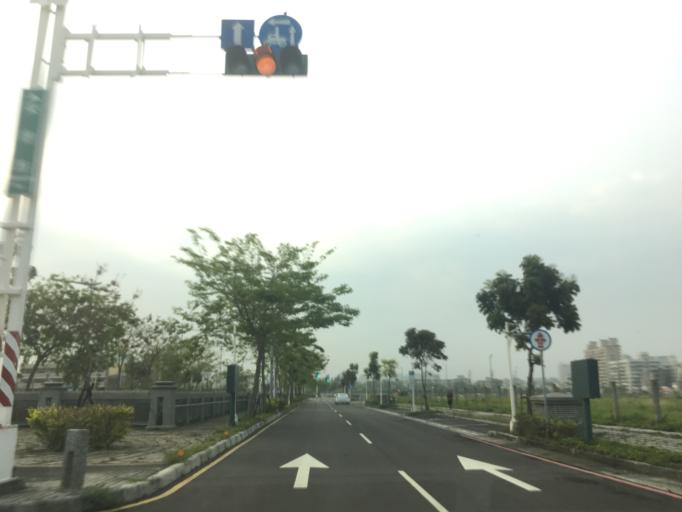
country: TW
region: Taiwan
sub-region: Taichung City
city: Taichung
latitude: 24.1929
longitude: 120.6688
